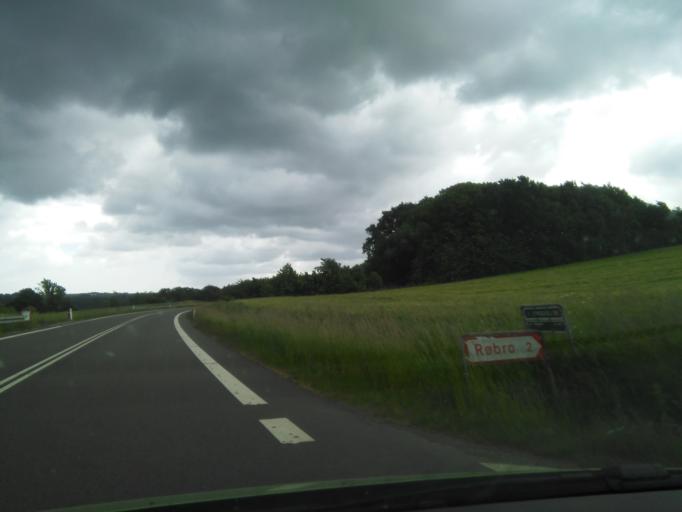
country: DK
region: Capital Region
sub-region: Bornholm Kommune
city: Akirkeby
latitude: 55.2167
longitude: 14.9245
